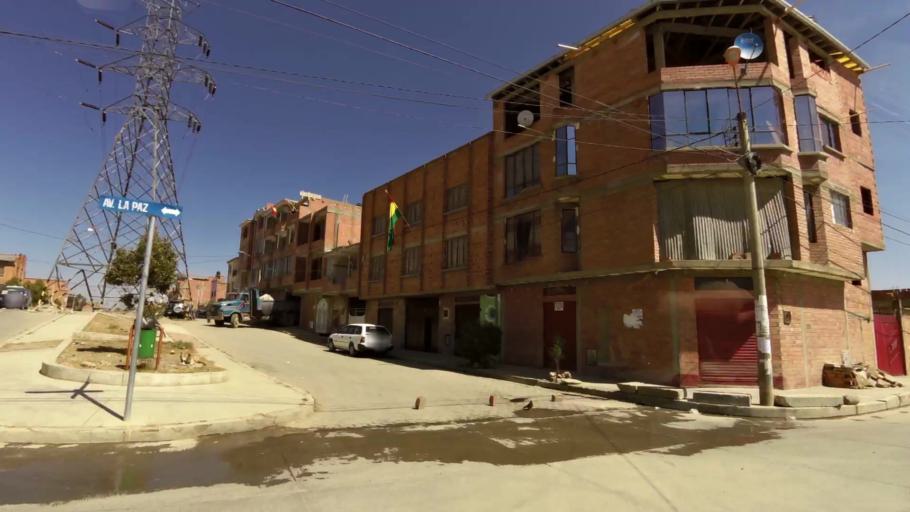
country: BO
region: La Paz
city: La Paz
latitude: -16.5348
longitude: -68.1533
